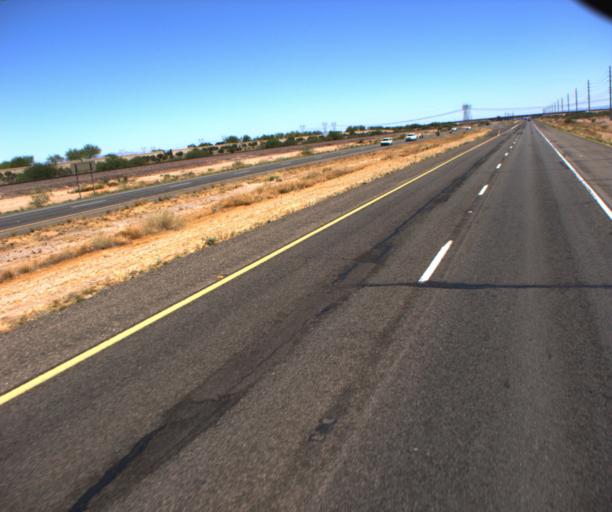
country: US
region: Arizona
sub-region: Maricopa County
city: Sun City West
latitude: 33.6933
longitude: -112.4205
